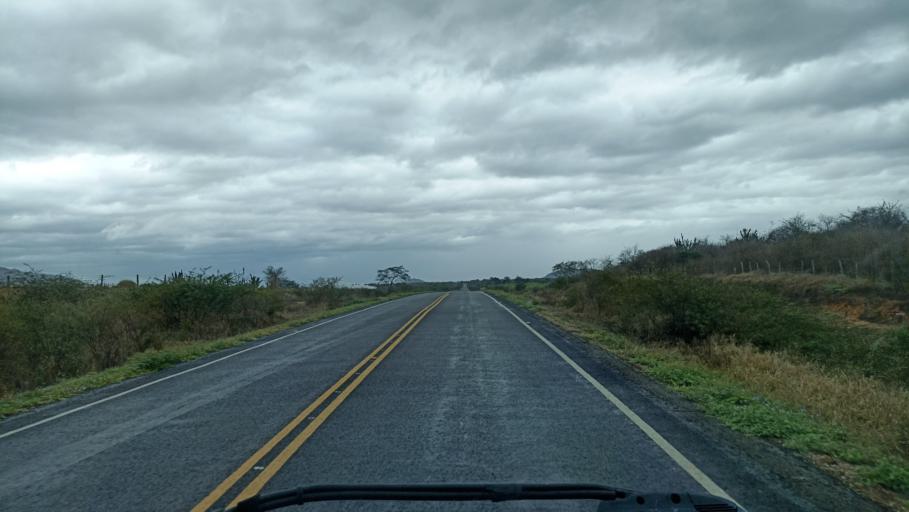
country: BR
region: Bahia
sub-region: Iacu
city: Iacu
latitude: -12.9684
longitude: -40.4954
